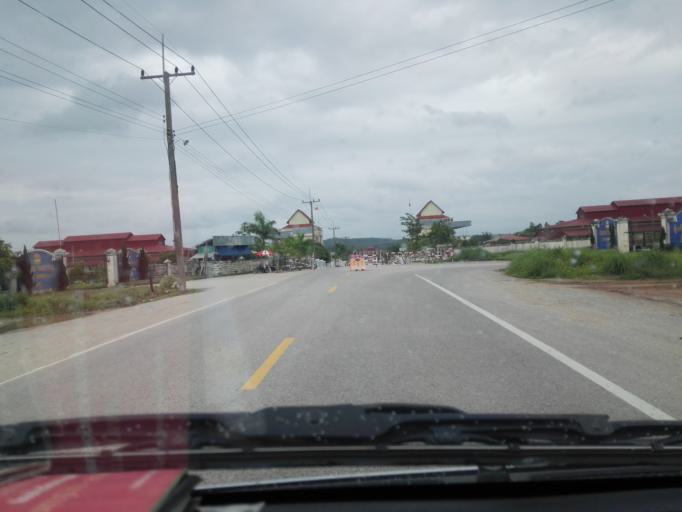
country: TH
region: Tak
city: Mae Sot
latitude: 16.6949
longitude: 98.4223
